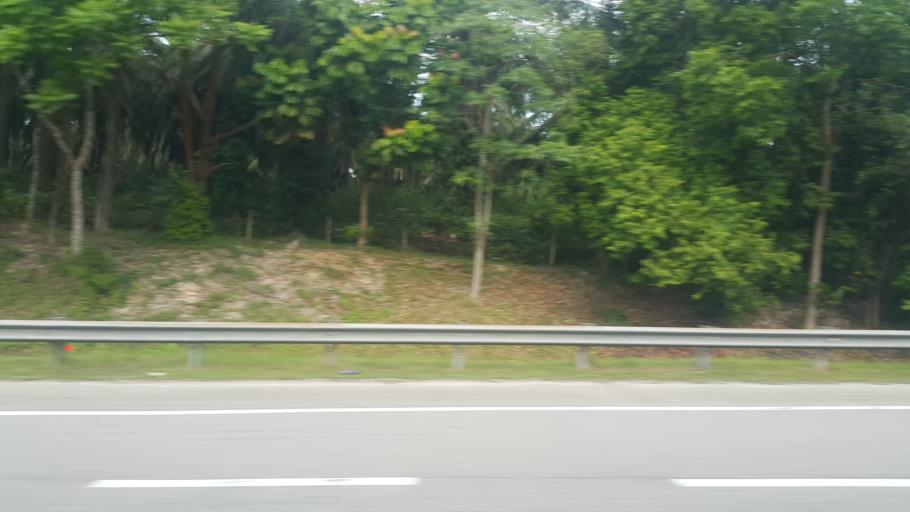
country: MY
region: Johor
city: Pekan Nenas
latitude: 1.4270
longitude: 103.6030
